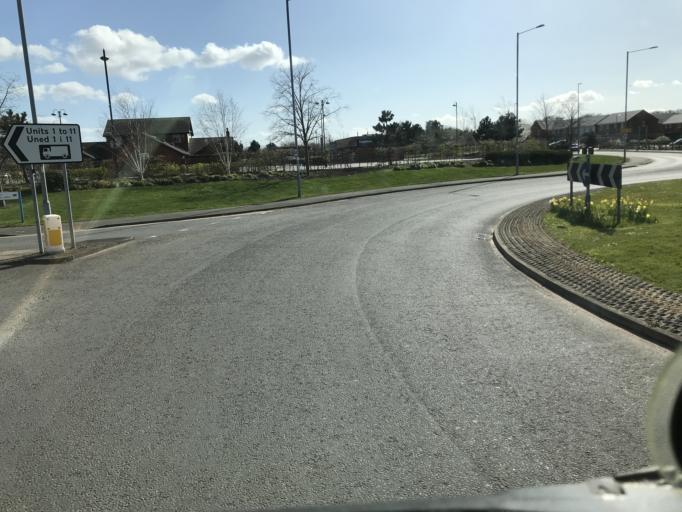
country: GB
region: Wales
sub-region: County of Flintshire
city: Hawarden
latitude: 53.1704
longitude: -2.9762
